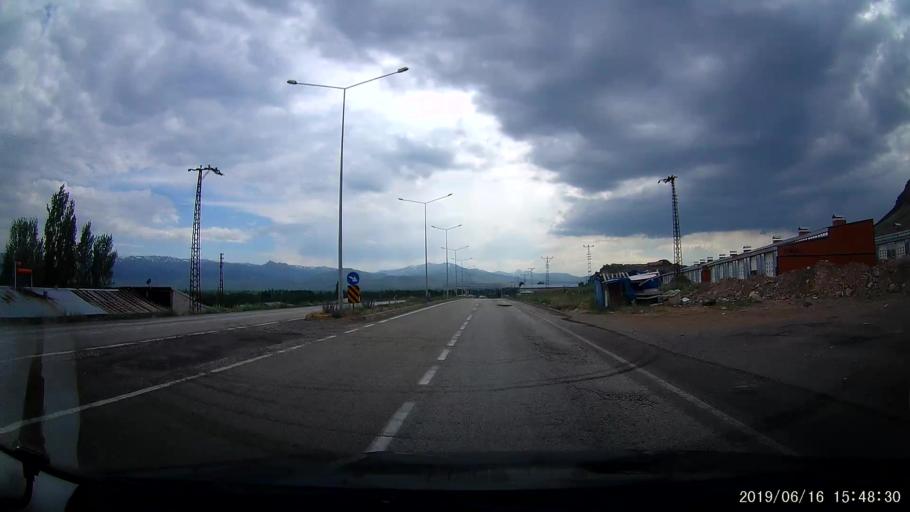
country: TR
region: Erzurum
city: Pasinler
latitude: 39.9824
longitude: 41.6999
